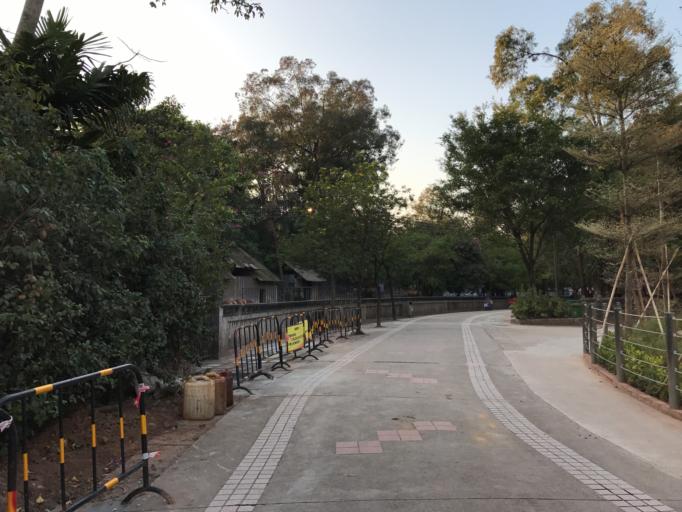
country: CN
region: Guangdong
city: Wushan
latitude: 23.1405
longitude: 113.3015
